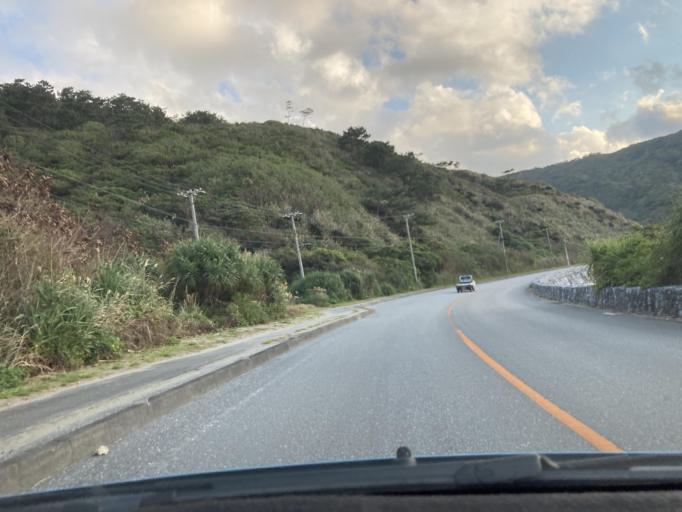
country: JP
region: Okinawa
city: Nago
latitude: 26.7703
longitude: 128.2053
